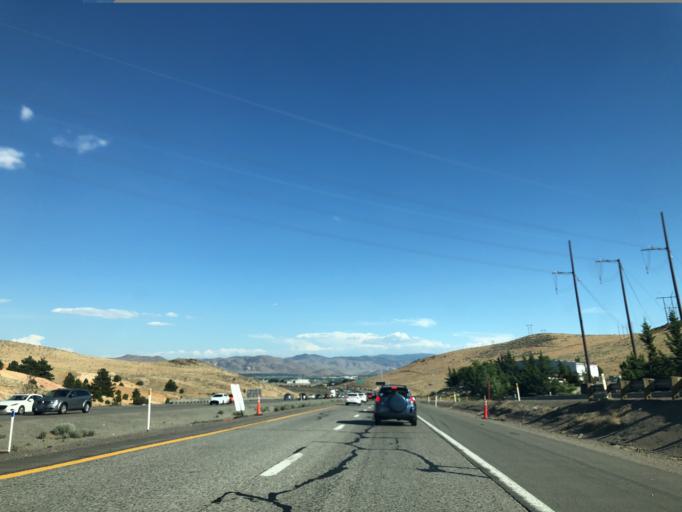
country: US
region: Nevada
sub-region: Washoe County
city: Sun Valley
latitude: 39.5708
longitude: -119.8064
